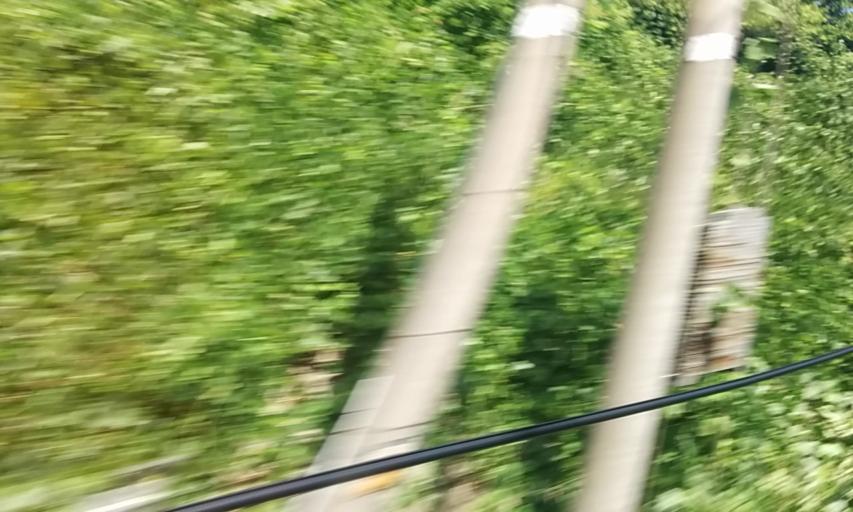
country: JP
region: Fukushima
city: Nihommatsu
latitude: 37.5439
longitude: 140.4469
